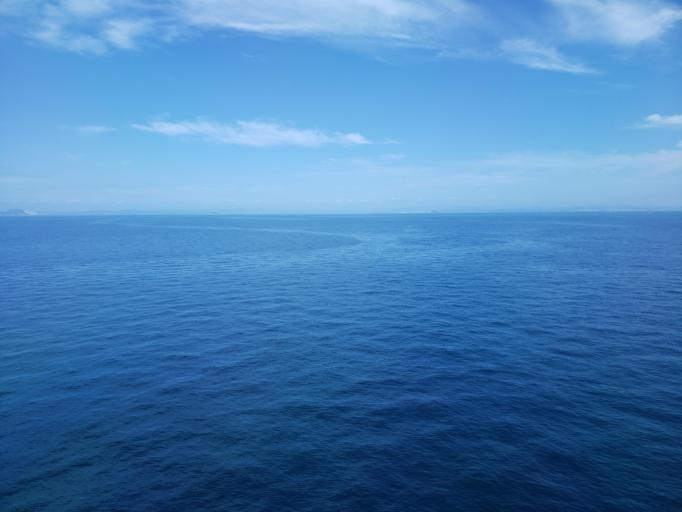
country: JP
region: Hyogo
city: Shirahamacho-usazakiminami
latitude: 34.5511
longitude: 134.7381
